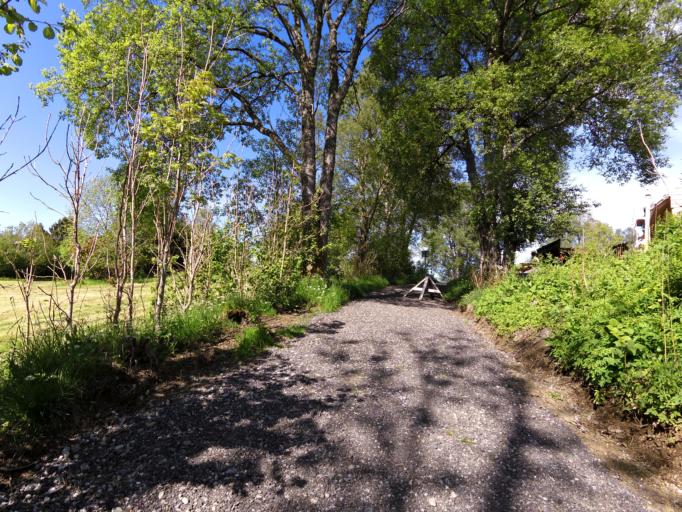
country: NO
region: Hordaland
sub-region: Stord
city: Leirvik
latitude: 59.7881
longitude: 5.4830
